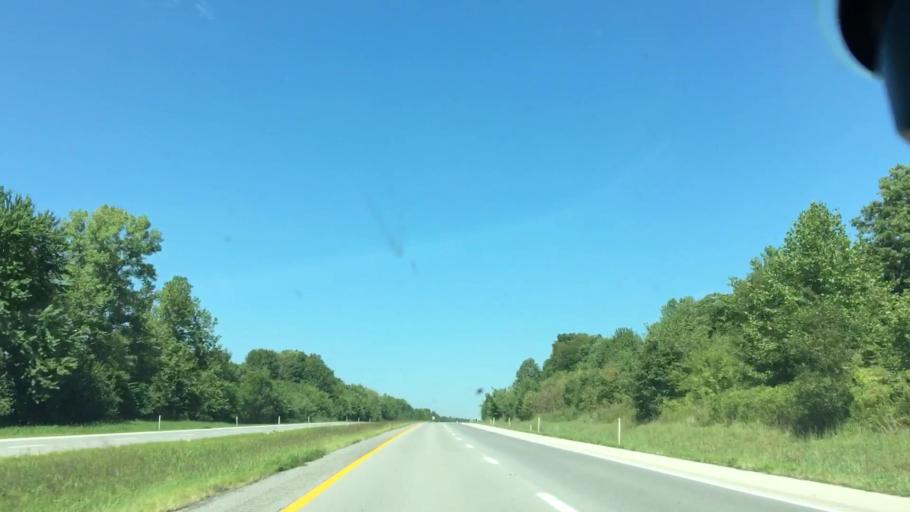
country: US
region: Kentucky
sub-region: Webster County
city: Sebree
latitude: 37.6533
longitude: -87.5125
